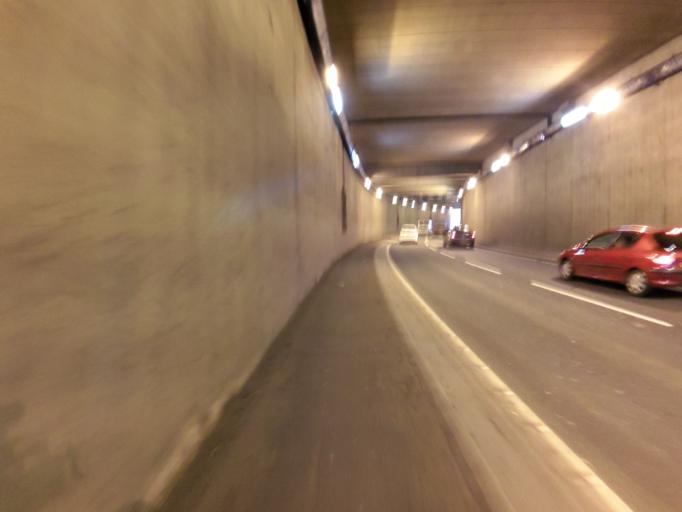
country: GB
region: England
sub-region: Doncaster
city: Doncaster
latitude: 53.5229
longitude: -1.1388
